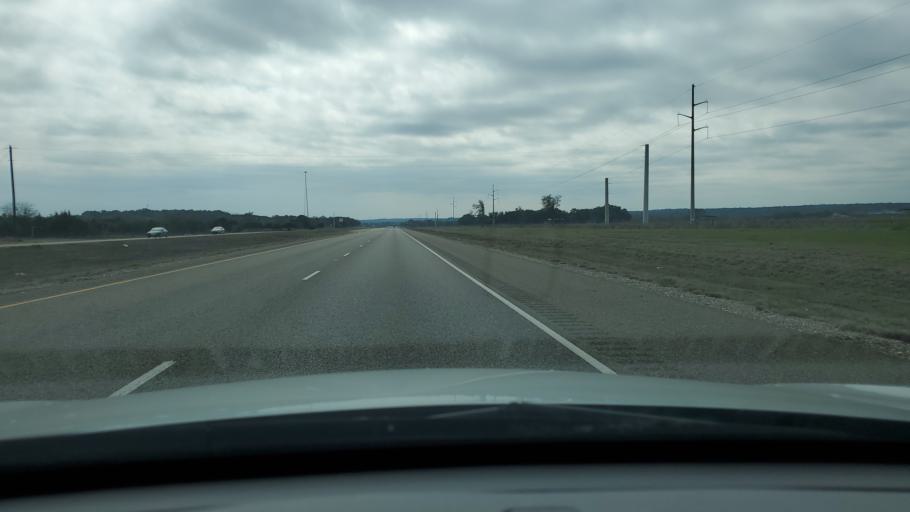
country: US
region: Texas
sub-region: Williamson County
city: Florence
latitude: 30.7835
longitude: -97.7630
